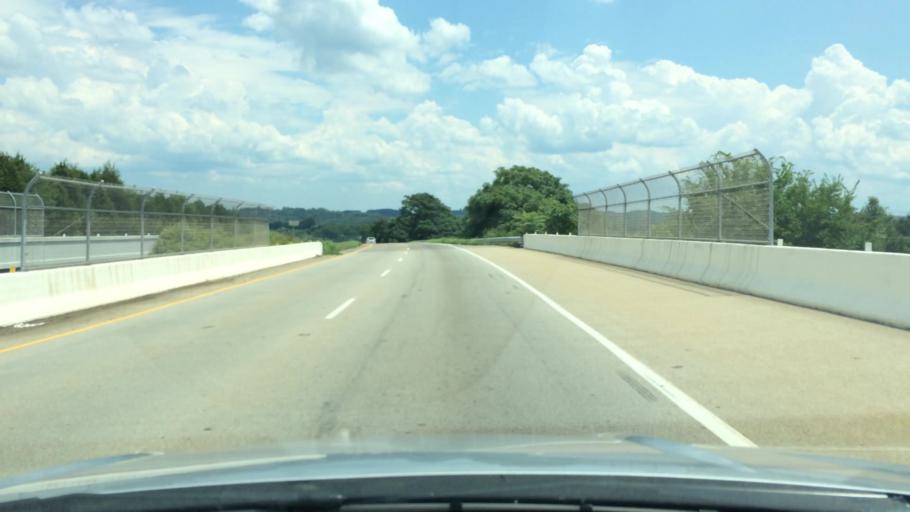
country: US
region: Tennessee
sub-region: Hamblen County
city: Morristown
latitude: 36.1707
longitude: -83.3858
